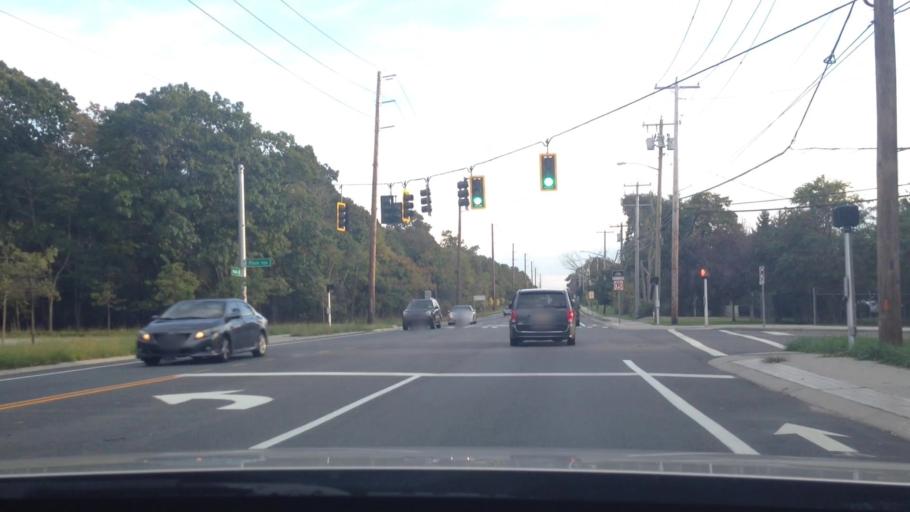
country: US
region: New York
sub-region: Suffolk County
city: Coram
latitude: 40.8607
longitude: -72.9988
